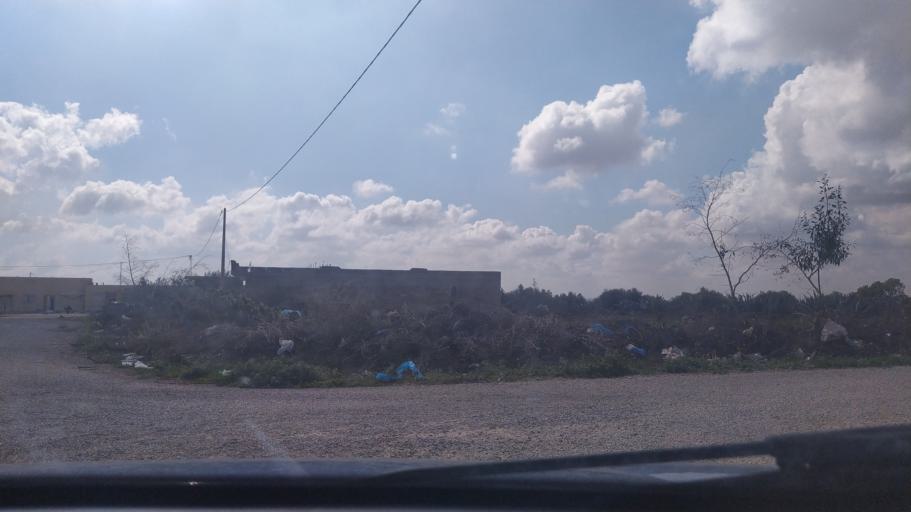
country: TN
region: Al Munastir
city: Sidi Bin Nur
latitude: 35.5279
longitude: 10.9432
